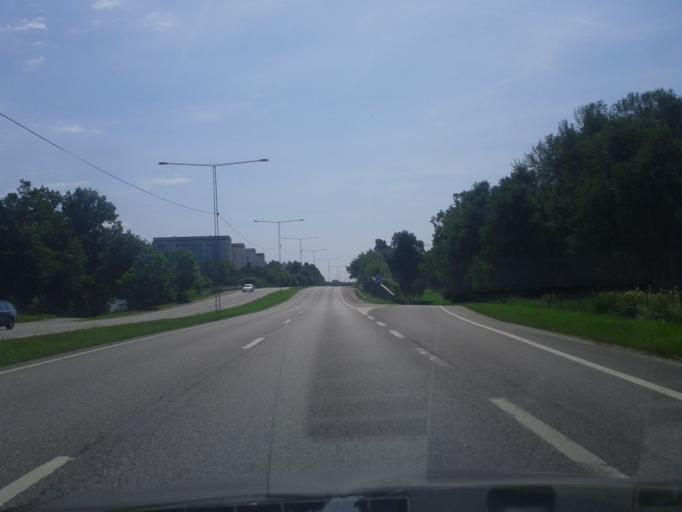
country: SE
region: Stockholm
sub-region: Huddinge Kommun
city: Huddinge
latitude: 59.2652
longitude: 18.0059
